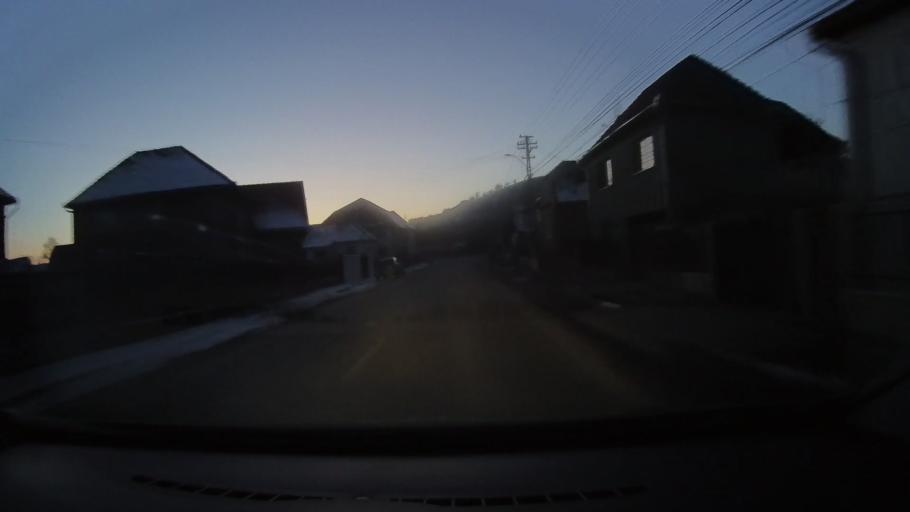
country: RO
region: Sibiu
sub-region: Comuna Darlos
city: Darlos
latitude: 46.1867
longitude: 24.3966
